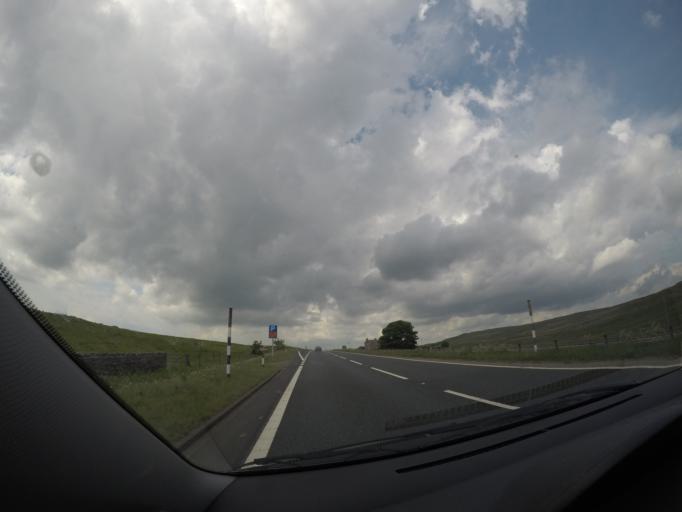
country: GB
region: England
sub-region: County Durham
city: Holwick
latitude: 54.5191
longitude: -2.2160
